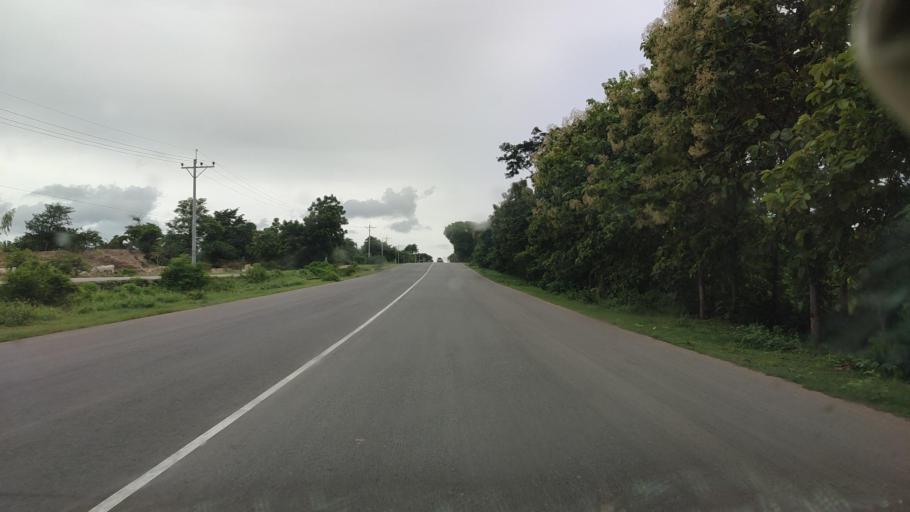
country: MM
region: Mandalay
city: Meiktila
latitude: 20.8001
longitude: 95.9101
